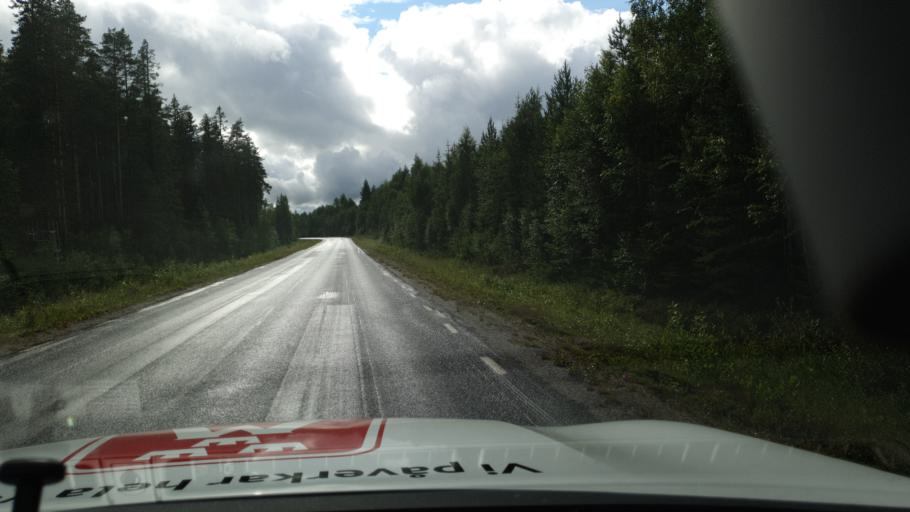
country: SE
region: Vaesterbotten
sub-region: Skelleftea Kommun
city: Soedra Bergsbyn
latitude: 64.5871
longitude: 21.0273
